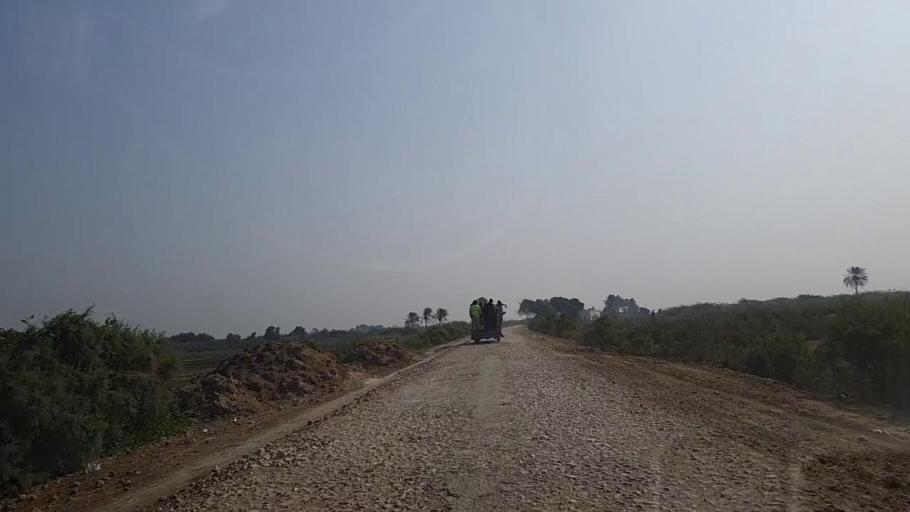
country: PK
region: Sindh
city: Keti Bandar
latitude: 24.2461
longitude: 67.6346
